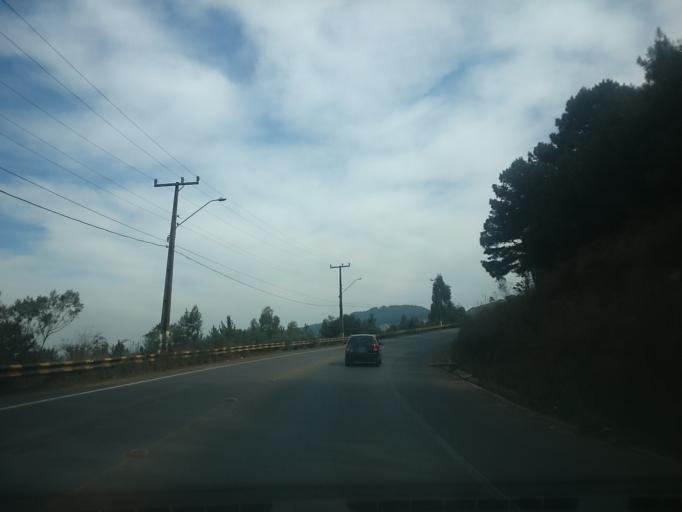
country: BR
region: Santa Catarina
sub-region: Lages
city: Lages
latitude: -27.8369
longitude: -50.3500
